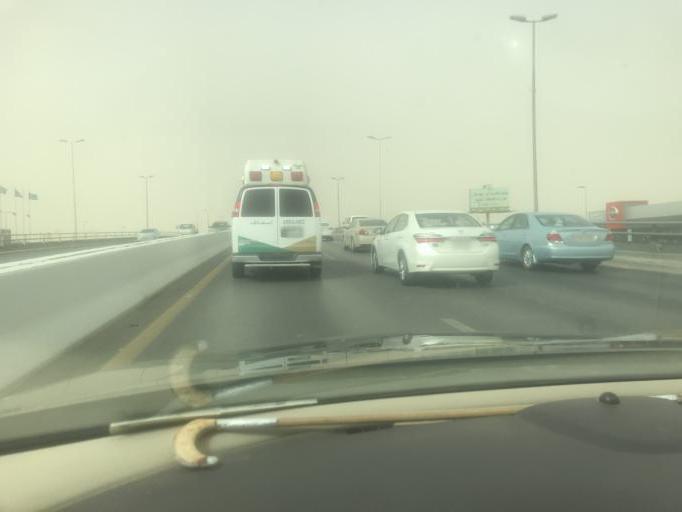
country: SA
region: Ar Riyad
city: Riyadh
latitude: 24.7025
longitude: 46.7433
